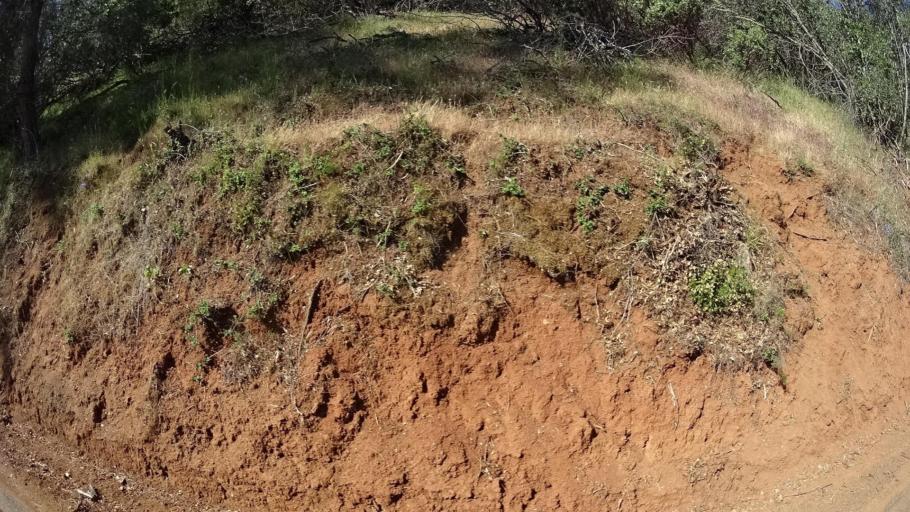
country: US
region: California
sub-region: Lake County
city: Clearlake Oaks
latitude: 39.0033
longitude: -122.7095
